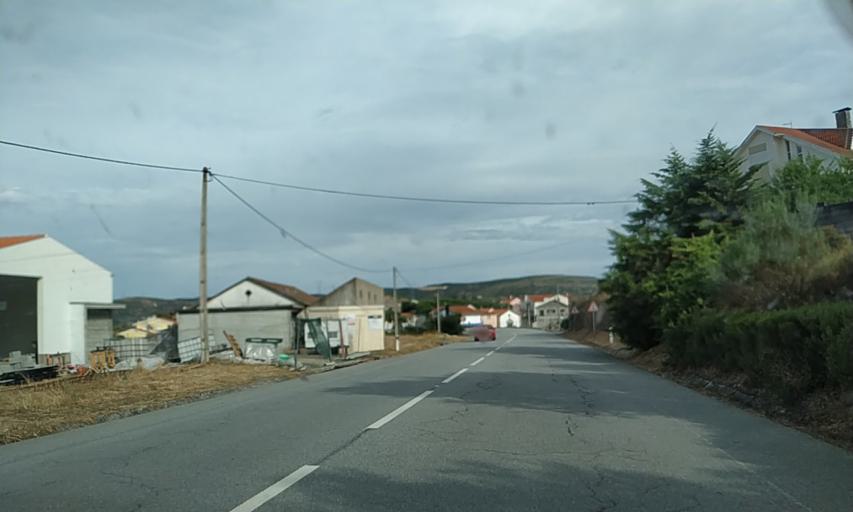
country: PT
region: Viseu
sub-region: Sao Joao da Pesqueira
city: Sao Joao da Pesqueira
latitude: 41.0989
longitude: -7.3807
